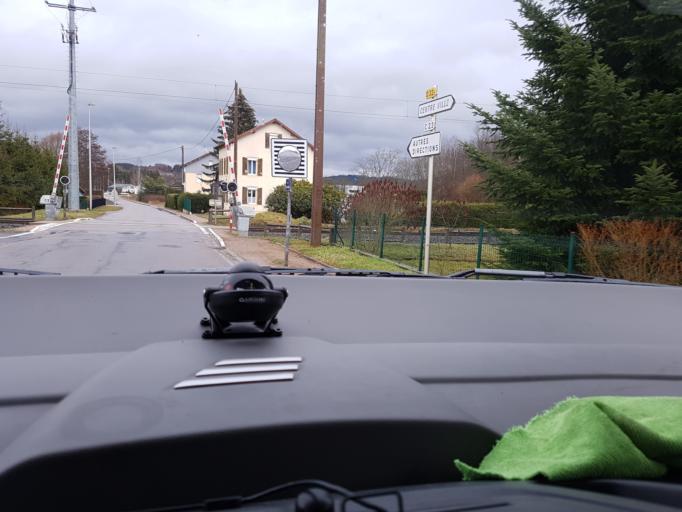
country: FR
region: Lorraine
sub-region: Departement des Vosges
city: Saint-Michel-sur-Meurthe
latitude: 48.3221
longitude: 6.8922
